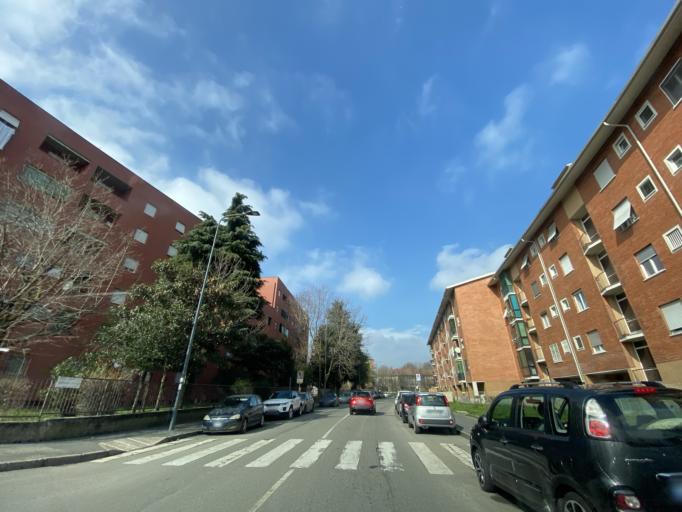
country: IT
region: Lombardy
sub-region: Citta metropolitana di Milano
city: Bresso
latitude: 45.5137
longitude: 9.1932
